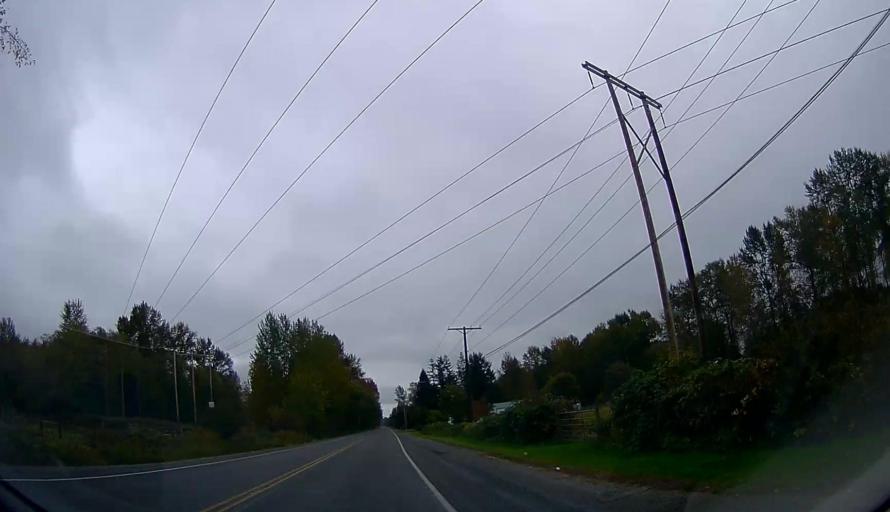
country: US
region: Washington
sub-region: Skagit County
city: Sedro-Woolley
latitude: 48.5239
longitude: -122.1677
